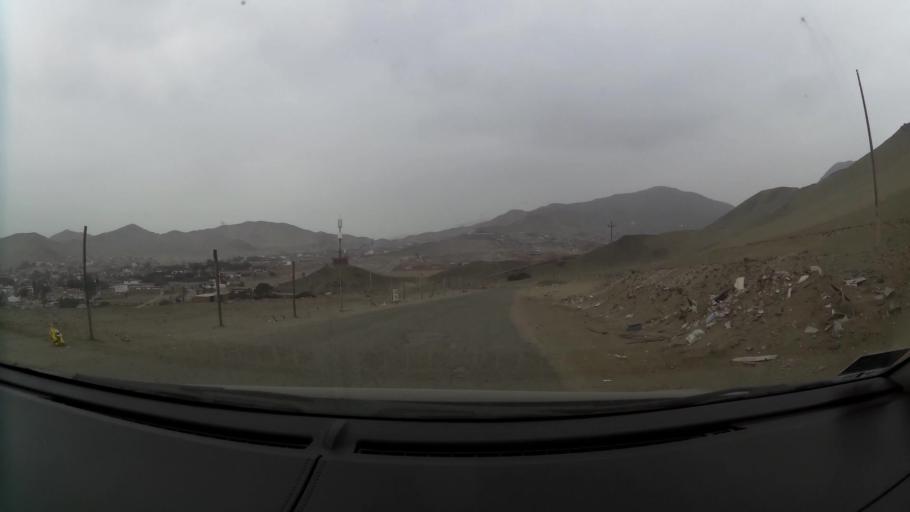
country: PE
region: Lima
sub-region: Lima
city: Santa Rosa
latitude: -11.8051
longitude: -77.1740
